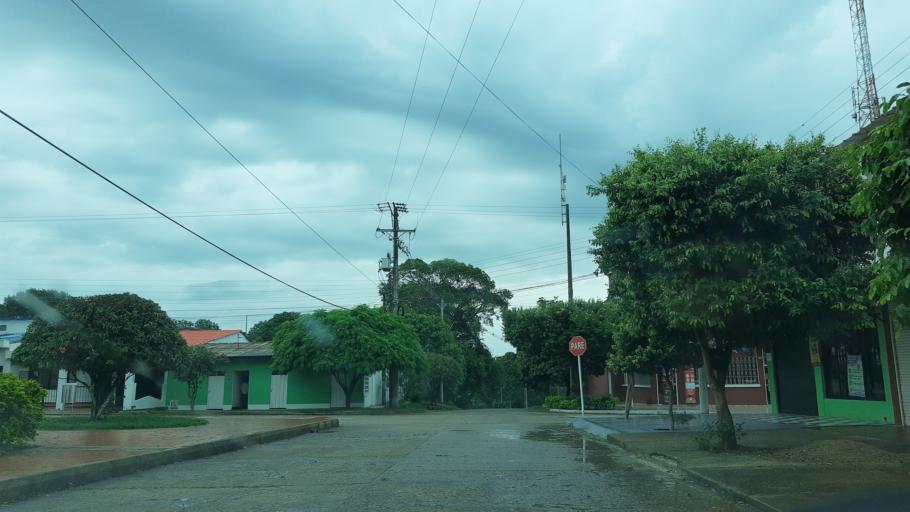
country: CO
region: Casanare
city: Monterrey
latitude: 4.8753
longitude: -72.8937
